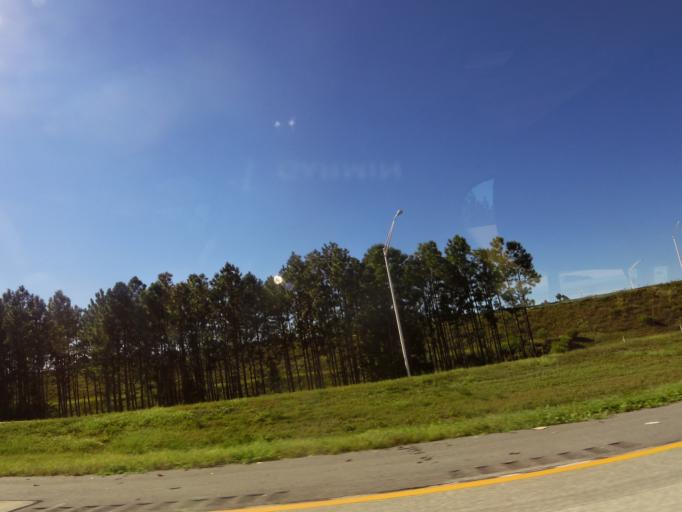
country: US
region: Florida
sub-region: Saint Johns County
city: Fruit Cove
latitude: 30.1175
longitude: -81.5132
